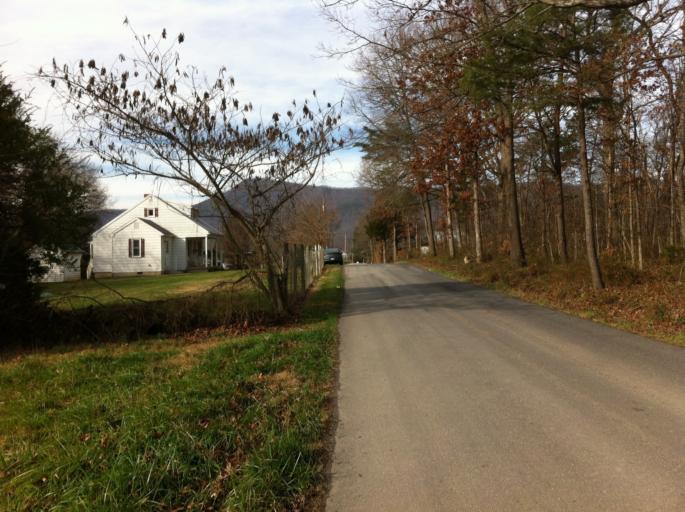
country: US
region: Virginia
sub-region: Page County
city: Luray
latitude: 38.7193
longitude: -78.4415
